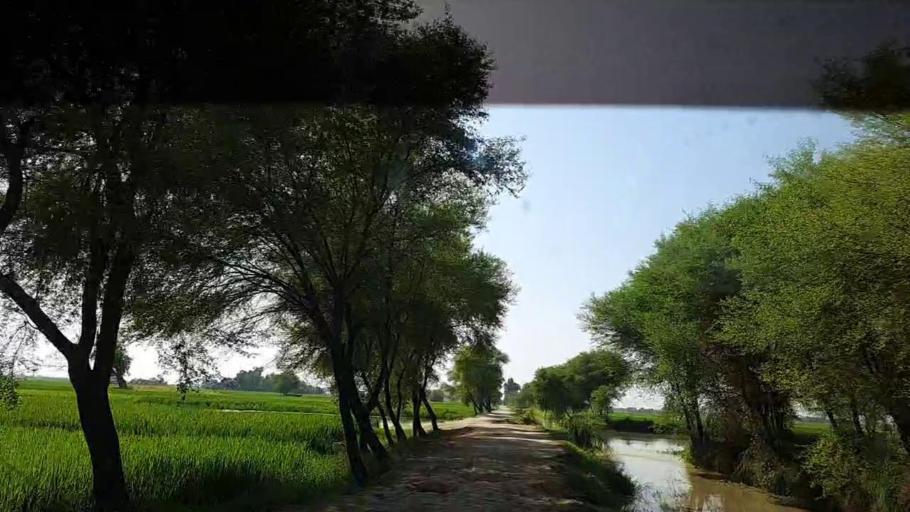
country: PK
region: Sindh
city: Ghauspur
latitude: 28.1761
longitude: 69.0450
